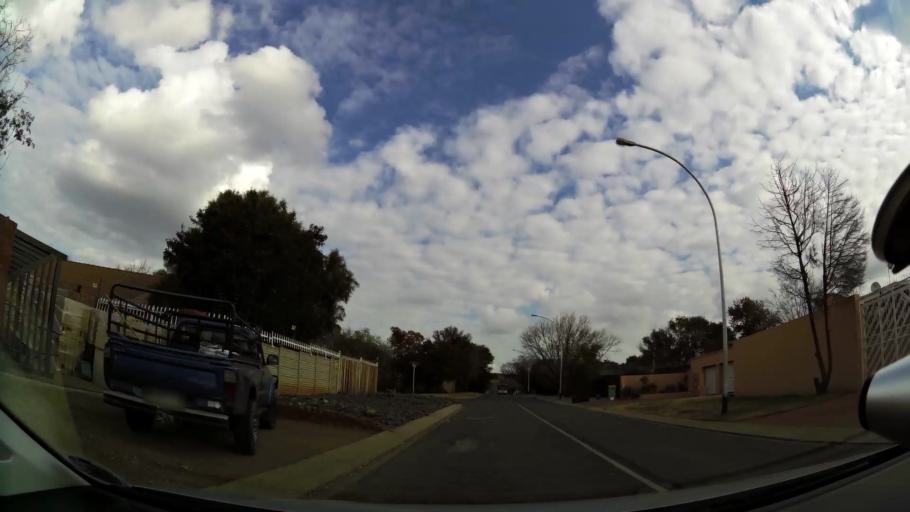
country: ZA
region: Orange Free State
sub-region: Mangaung Metropolitan Municipality
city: Bloemfontein
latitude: -29.0712
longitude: 26.2094
